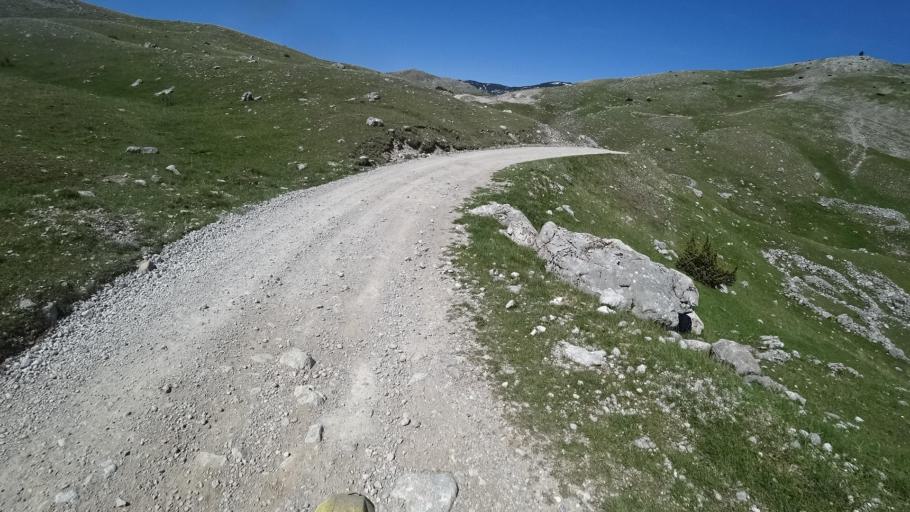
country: BA
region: Federation of Bosnia and Herzegovina
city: Gracanica
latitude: 43.6855
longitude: 18.2339
